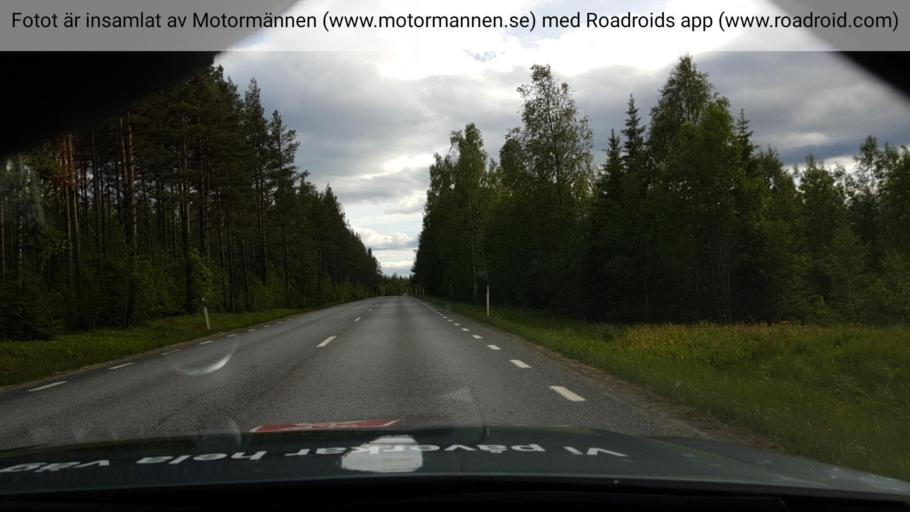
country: SE
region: Jaemtland
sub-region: Stroemsunds Kommun
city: Stroemsund
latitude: 63.5309
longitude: 15.3308
